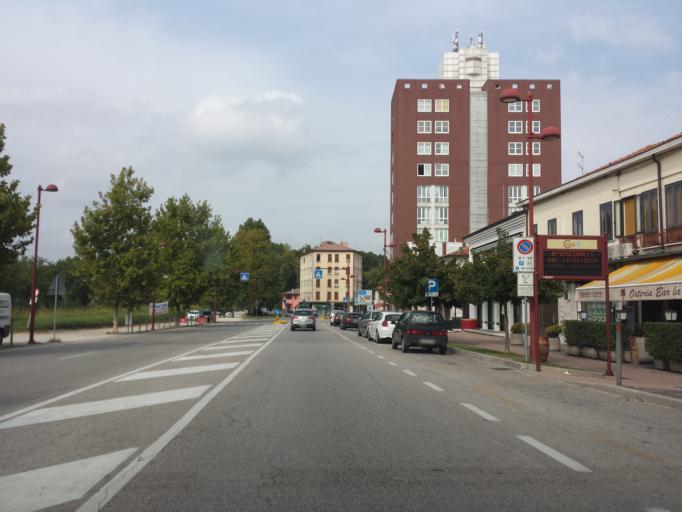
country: IT
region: Veneto
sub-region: Provincia di Padova
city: Mejaniga
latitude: 45.4494
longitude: 11.8967
